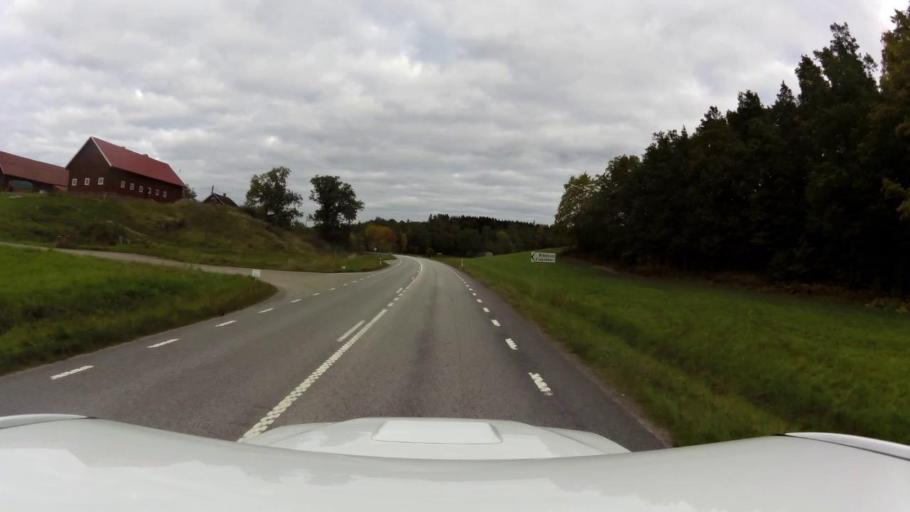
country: SE
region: OEstergoetland
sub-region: Kinda Kommun
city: Rimforsa
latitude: 58.1805
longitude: 15.6736
